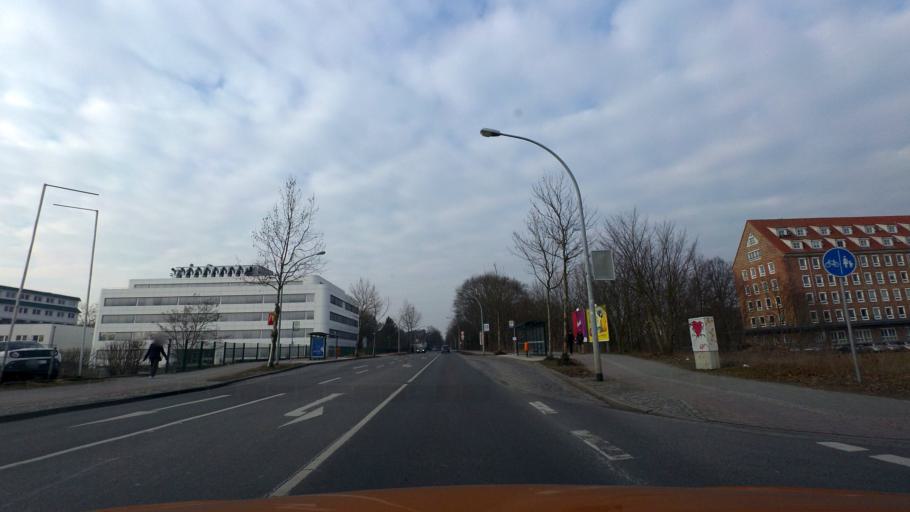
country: DE
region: Brandenburg
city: Kleinmachnow
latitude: 52.4000
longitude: 13.2408
